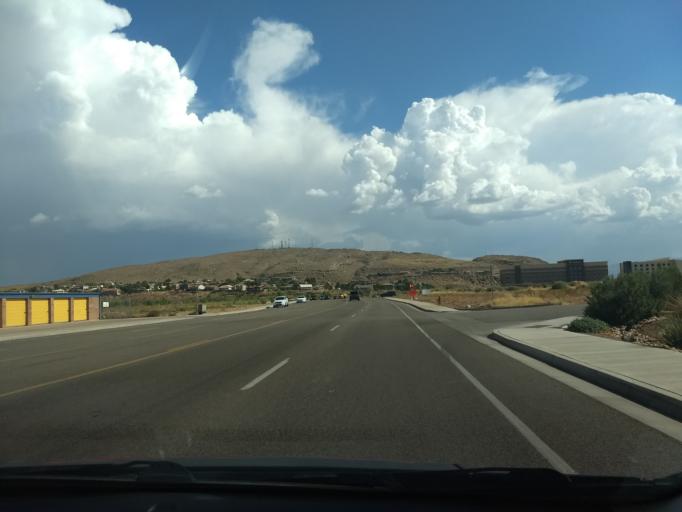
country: US
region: Utah
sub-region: Washington County
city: Saint George
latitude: 37.0809
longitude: -113.5780
